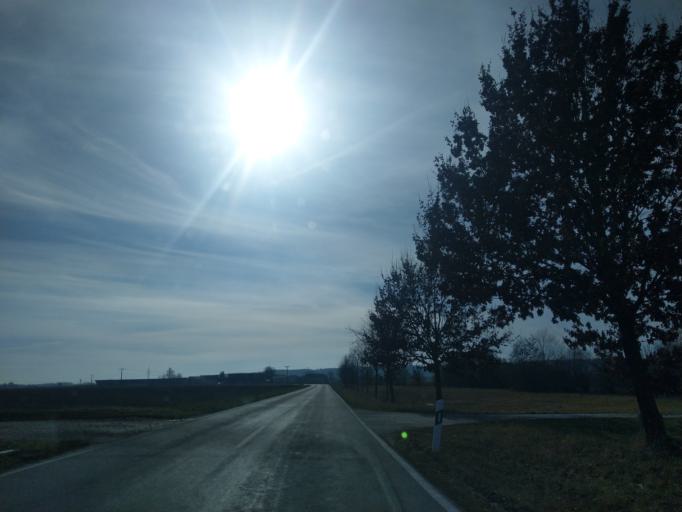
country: DE
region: Bavaria
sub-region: Lower Bavaria
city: Buchhofen
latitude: 48.6766
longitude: 12.9629
